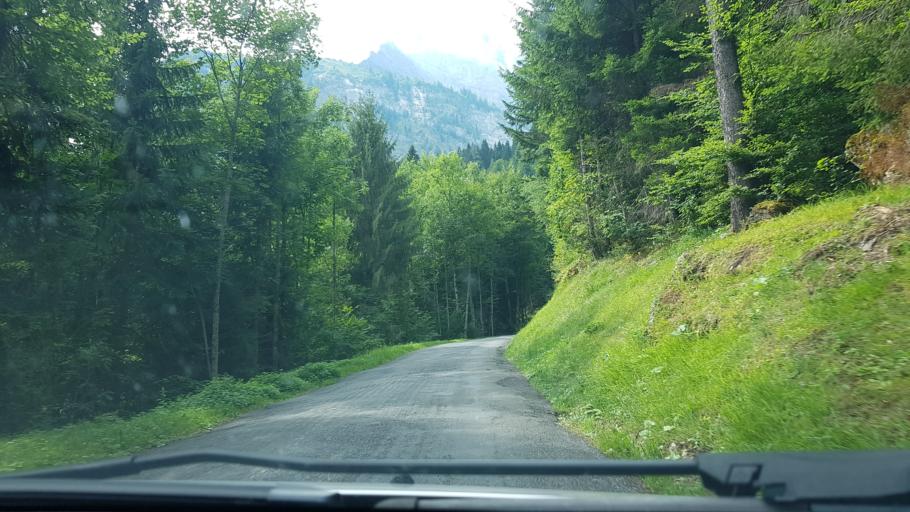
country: FR
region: Rhone-Alpes
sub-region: Departement de la Haute-Savoie
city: Samoens
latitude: 46.0318
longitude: 6.7702
